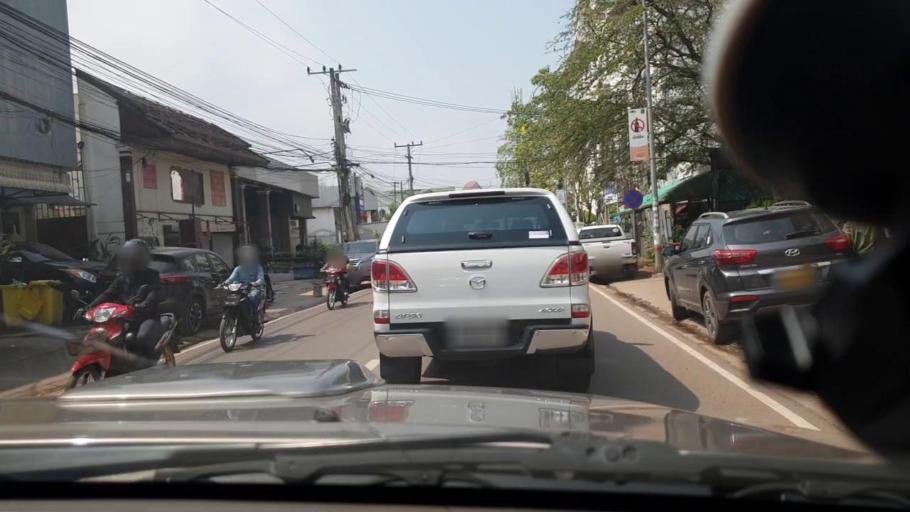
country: LA
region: Vientiane
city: Vientiane
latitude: 17.9570
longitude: 102.6228
